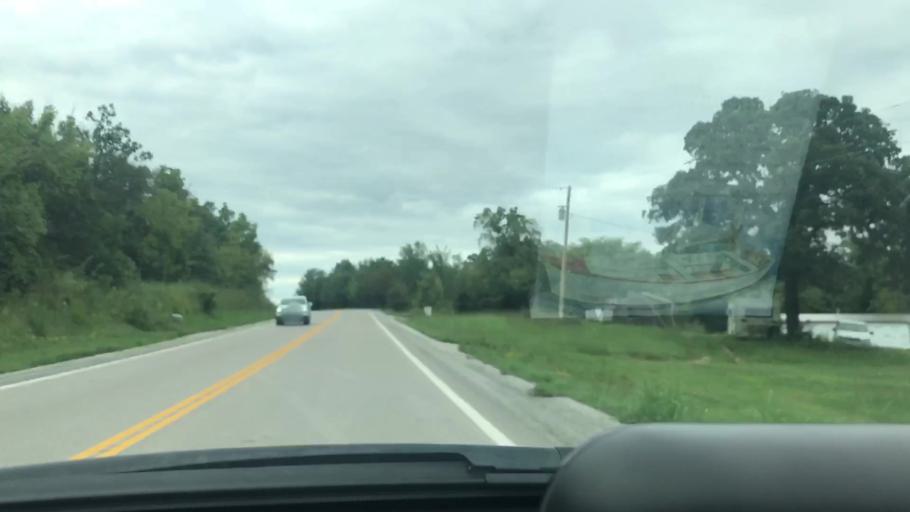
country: US
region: Missouri
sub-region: Benton County
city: Warsaw
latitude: 38.1680
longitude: -93.3094
